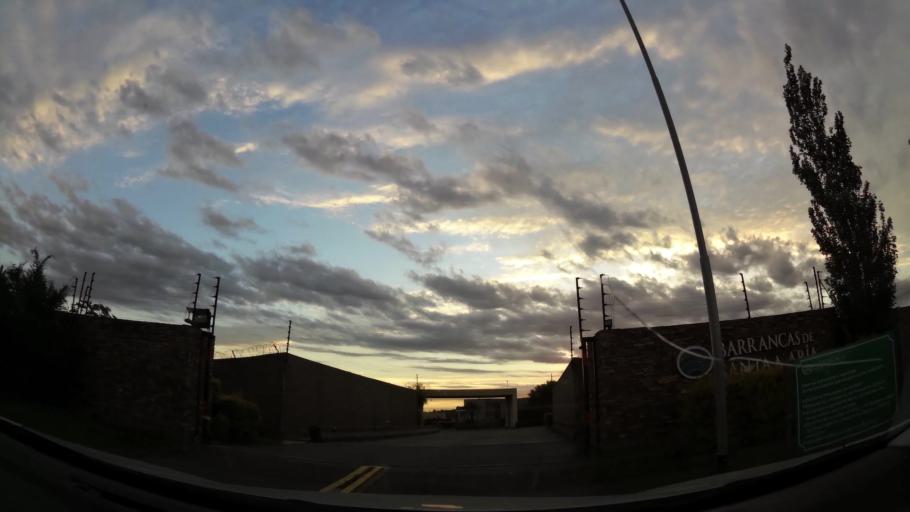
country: AR
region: Buenos Aires
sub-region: Partido de Tigre
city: Tigre
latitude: -34.4444
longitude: -58.6535
